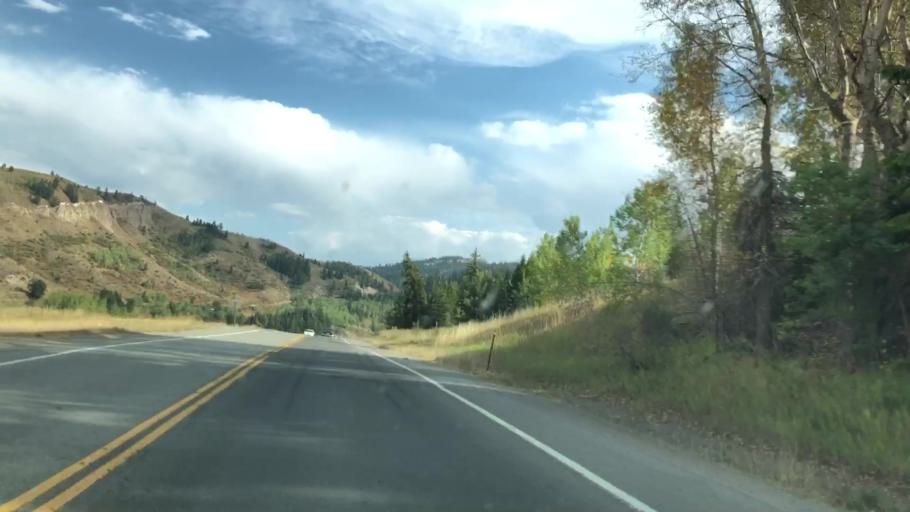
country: US
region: Wyoming
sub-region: Teton County
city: South Park
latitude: 43.3584
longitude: -110.7244
